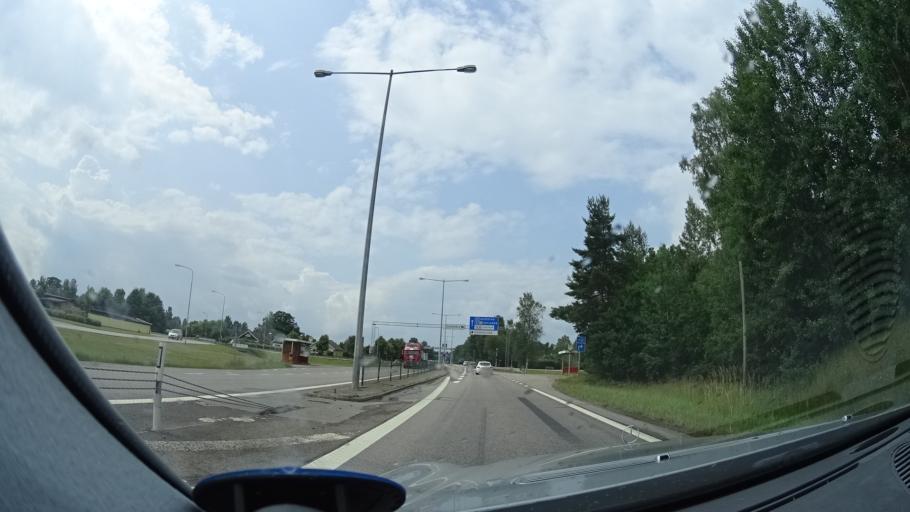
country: SE
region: Kalmar
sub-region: Nybro Kommun
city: Nybro
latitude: 56.7335
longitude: 15.9461
